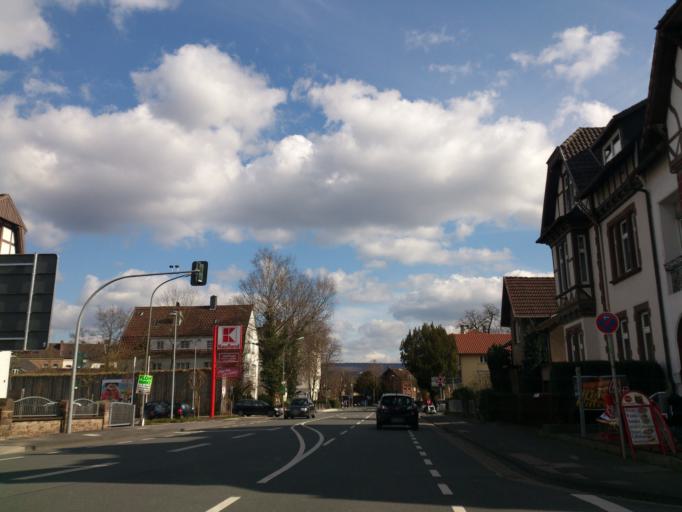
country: DE
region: North Rhine-Westphalia
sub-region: Regierungsbezirk Detmold
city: Hoexter
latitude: 51.7787
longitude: 9.3794
